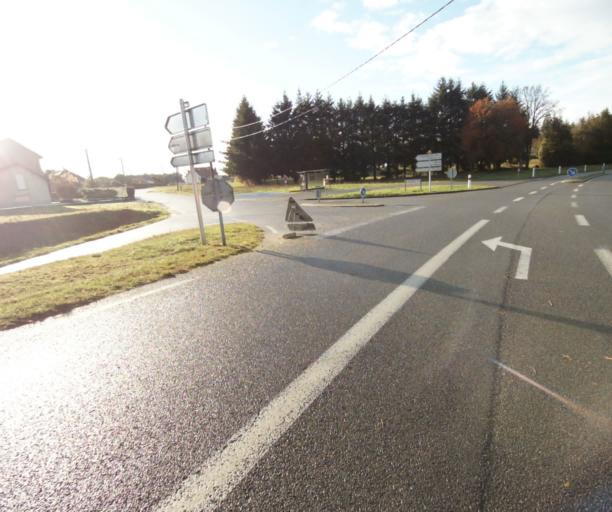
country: FR
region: Limousin
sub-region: Departement de la Correze
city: Saint-Mexant
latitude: 45.2458
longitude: 1.6281
